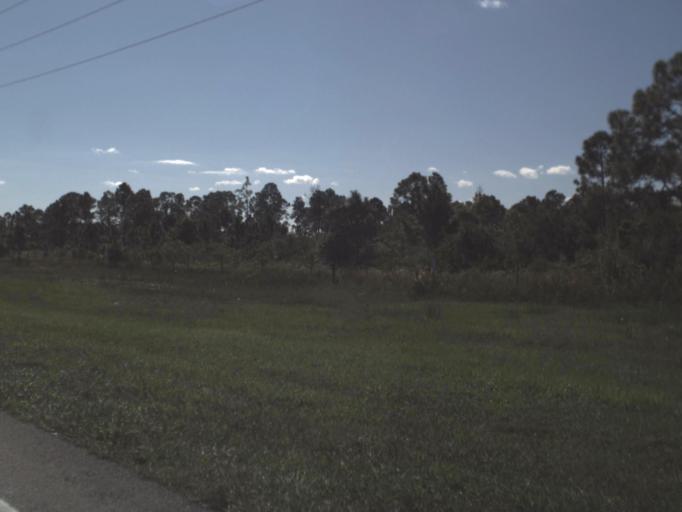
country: US
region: Florida
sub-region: Lee County
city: Gateway
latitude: 26.5735
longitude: -81.6947
